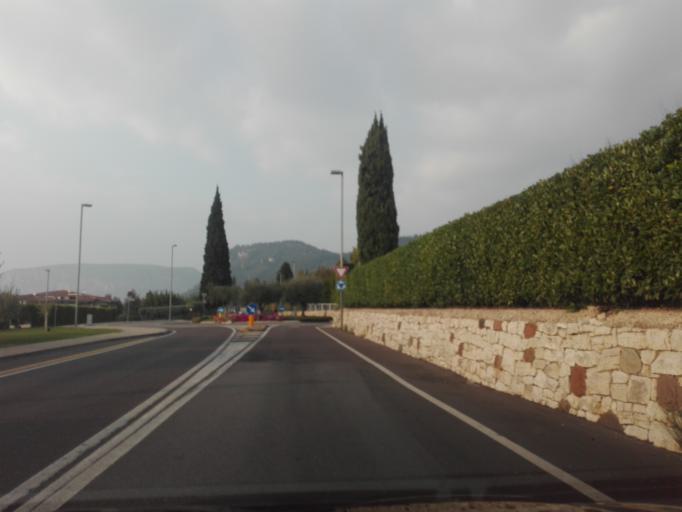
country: IT
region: Veneto
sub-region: Provincia di Verona
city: Bardolino
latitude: 45.5539
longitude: 10.7204
